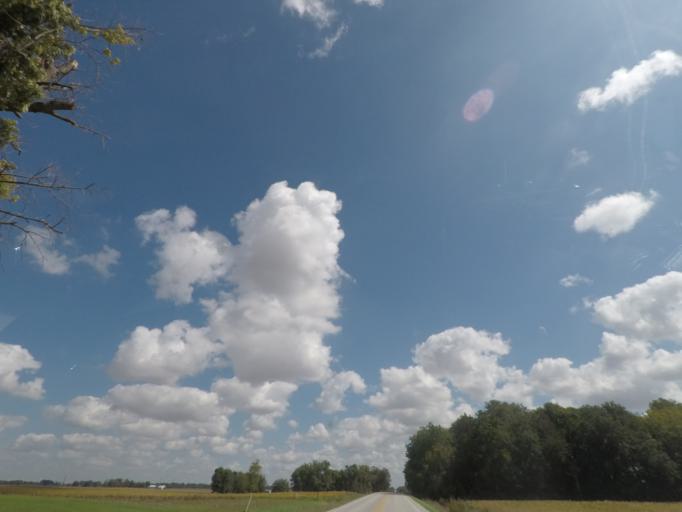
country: US
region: Iowa
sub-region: Story County
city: Nevada
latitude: 42.0779
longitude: -93.3777
